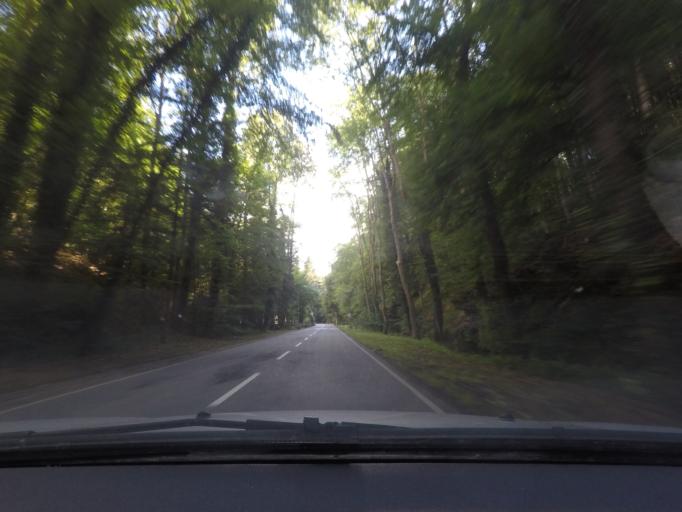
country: LU
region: Luxembourg
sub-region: Canton de Mersch
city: Heffingen
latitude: 49.7507
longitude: 6.2694
